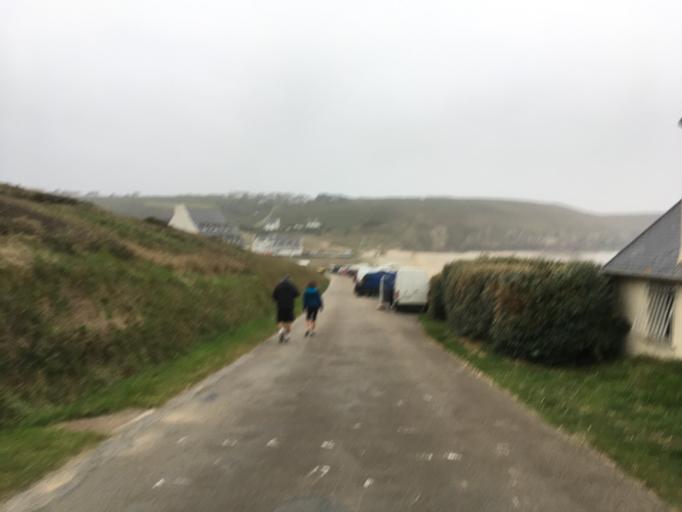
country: FR
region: Brittany
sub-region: Departement du Finistere
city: Plogoff
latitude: 48.0495
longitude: -4.7048
